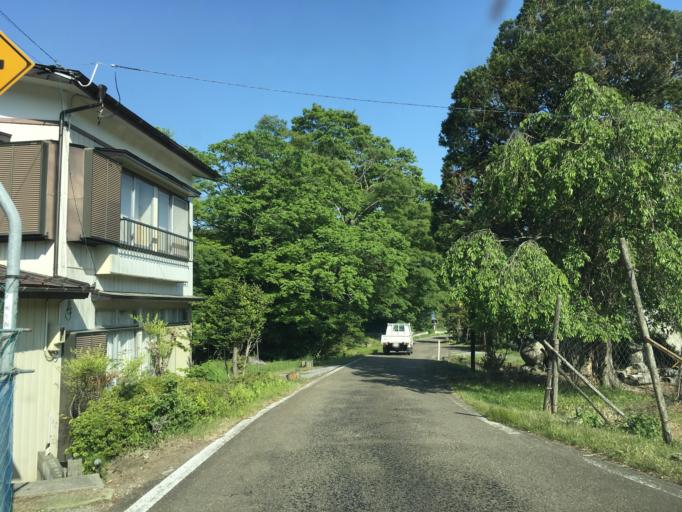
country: JP
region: Iwate
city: Kamaishi
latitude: 39.1970
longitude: 141.8349
